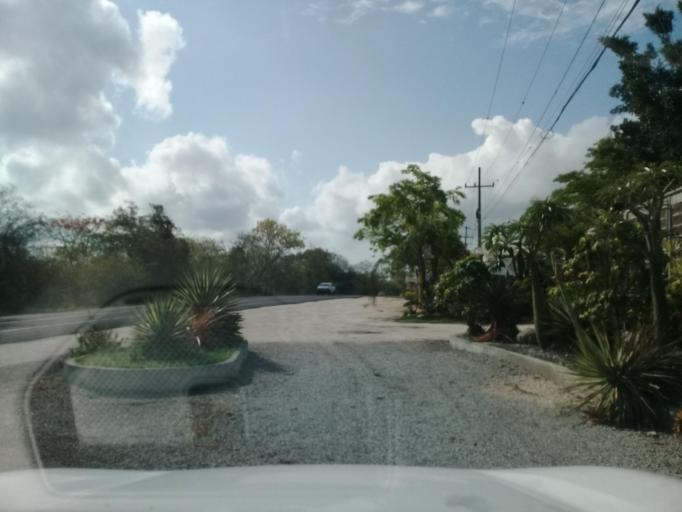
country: MX
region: Veracruz
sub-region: Emiliano Zapata
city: Plan del Rio
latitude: 19.4121
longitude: -96.6521
